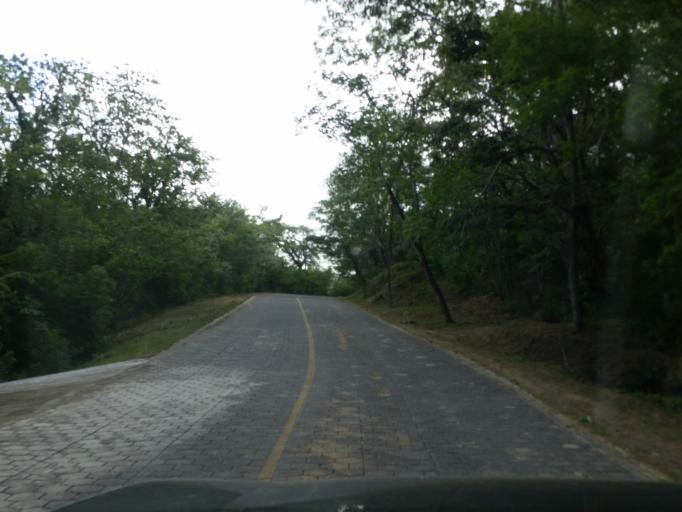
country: NI
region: Rivas
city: San Juan del Sur
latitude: 11.2346
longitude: -85.8283
